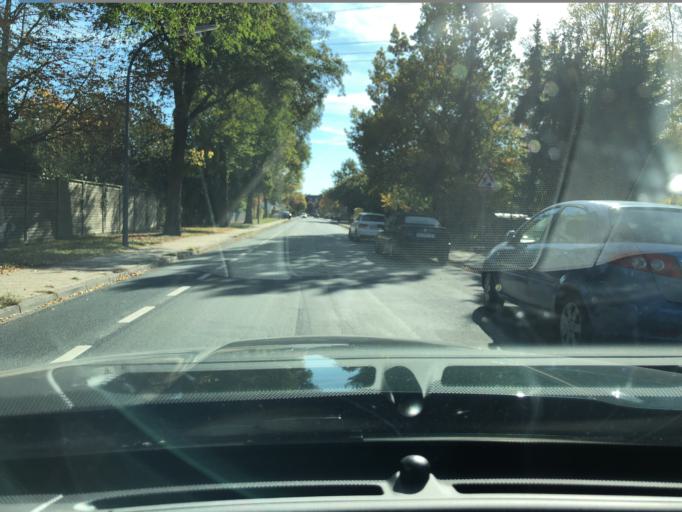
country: DE
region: Lower Saxony
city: Hasbergen
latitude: 52.2614
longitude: 7.9863
